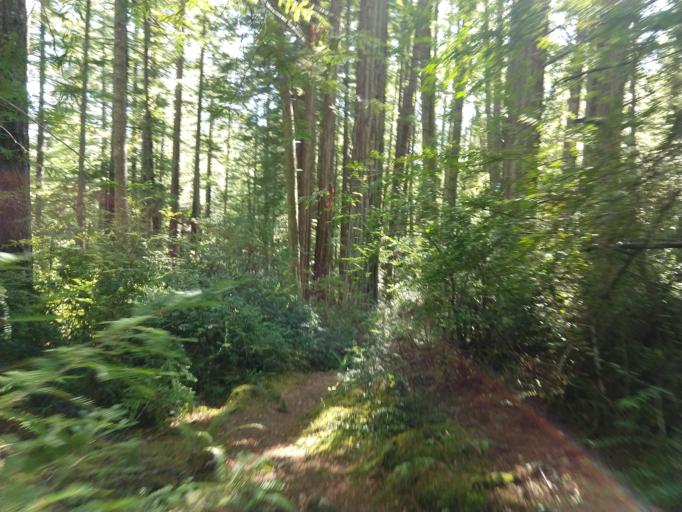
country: US
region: California
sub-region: Humboldt County
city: Rio Dell
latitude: 40.3577
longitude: -123.9945
